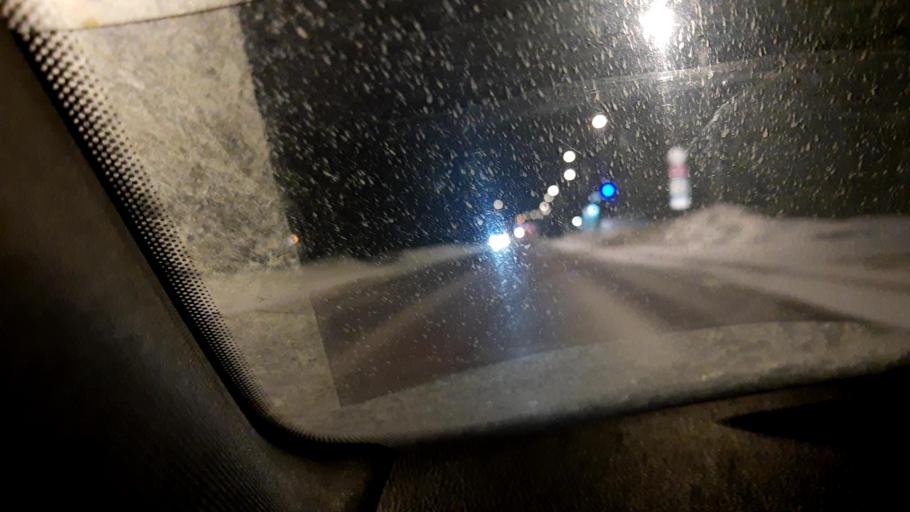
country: RU
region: Moskovskaya
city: Peresvet
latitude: 56.4438
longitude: 38.0985
